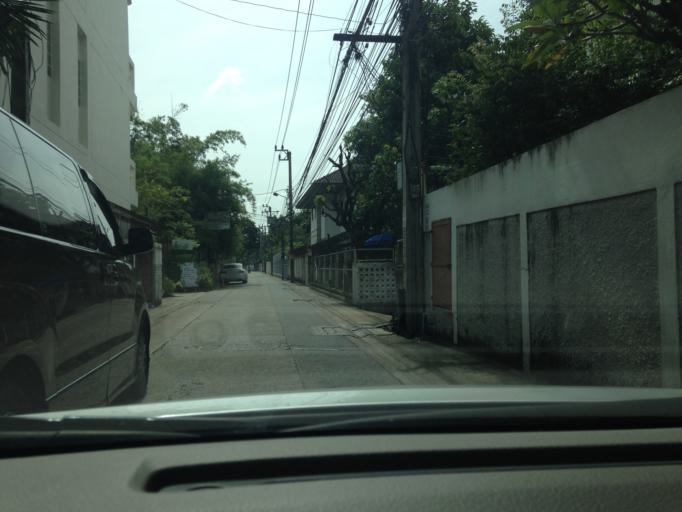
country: TH
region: Bangkok
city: Phaya Thai
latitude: 13.7809
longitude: 100.5418
